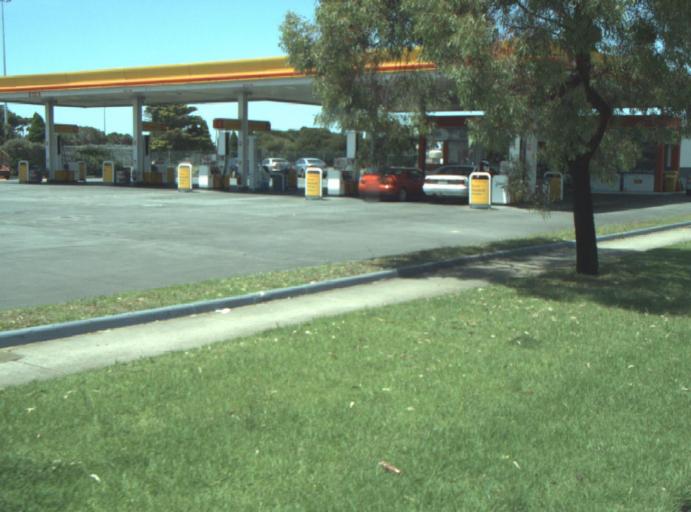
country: AU
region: Victoria
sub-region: Greater Geelong
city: Bell Park
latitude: -38.1168
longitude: 144.3543
